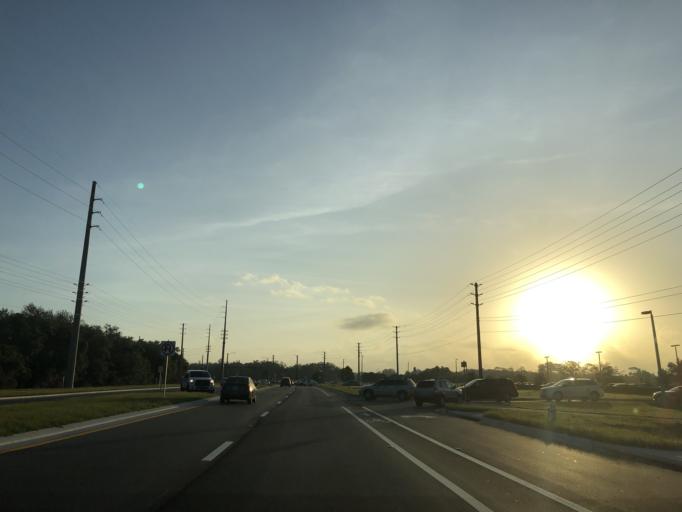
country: US
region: Florida
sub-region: Osceola County
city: Kissimmee
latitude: 28.3247
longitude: -81.4289
